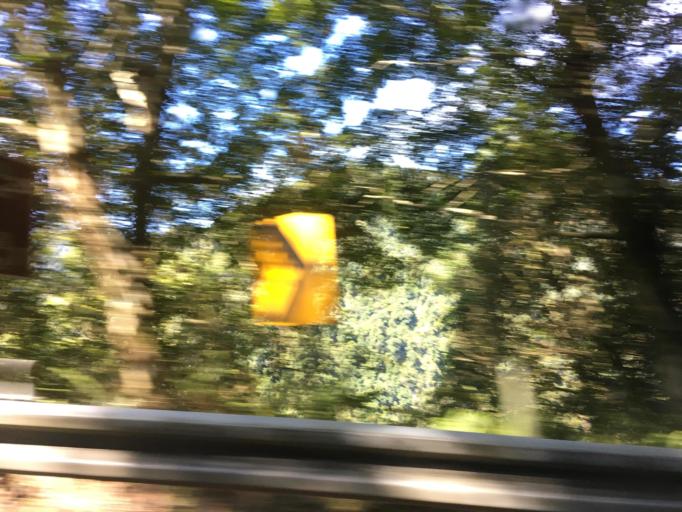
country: TW
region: Taiwan
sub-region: Yilan
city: Yilan
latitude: 24.5544
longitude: 121.5074
